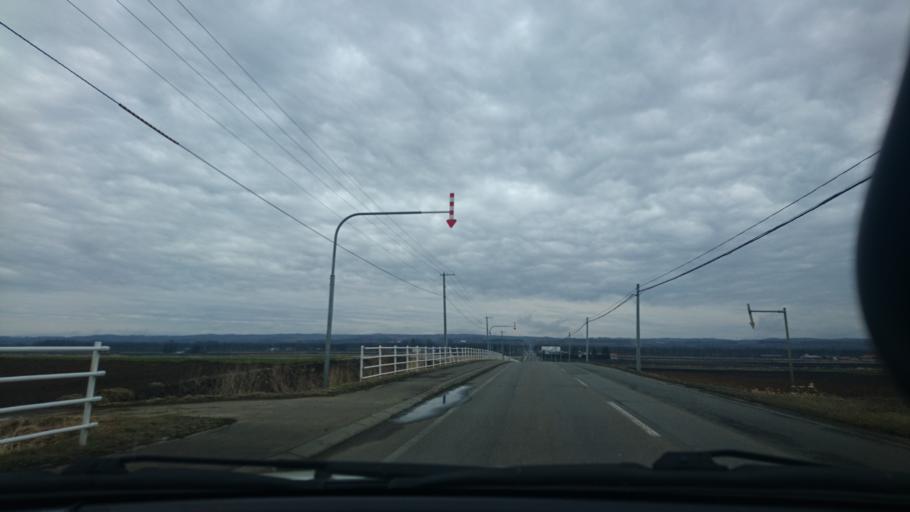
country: JP
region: Hokkaido
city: Otofuke
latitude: 42.9938
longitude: 143.2247
